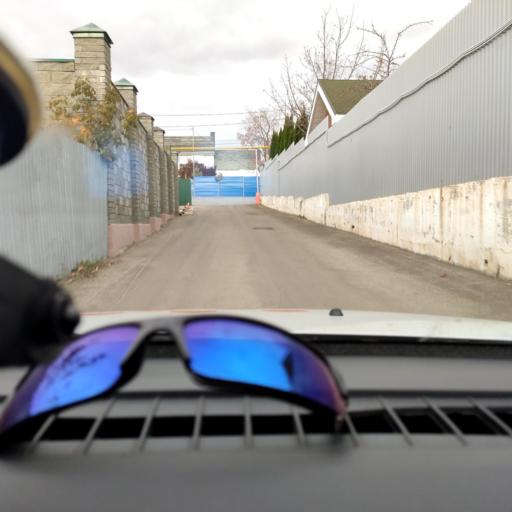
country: RU
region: Samara
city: Samara
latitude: 53.2366
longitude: 50.1732
